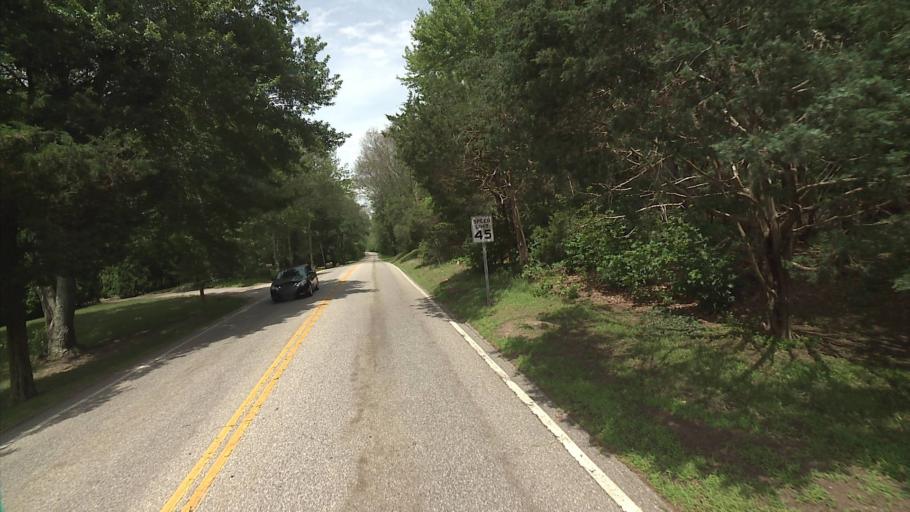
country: US
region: Connecticut
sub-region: New London County
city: Preston City
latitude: 41.5685
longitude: -71.9688
